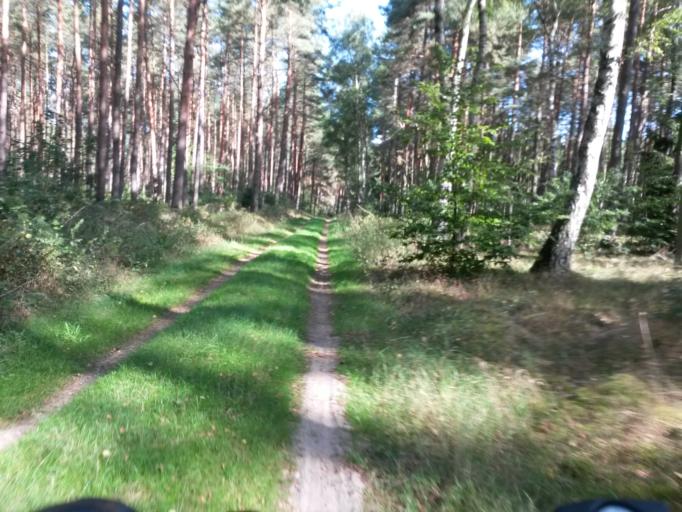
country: DE
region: Brandenburg
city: Lychen
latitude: 53.1546
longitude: 13.3744
